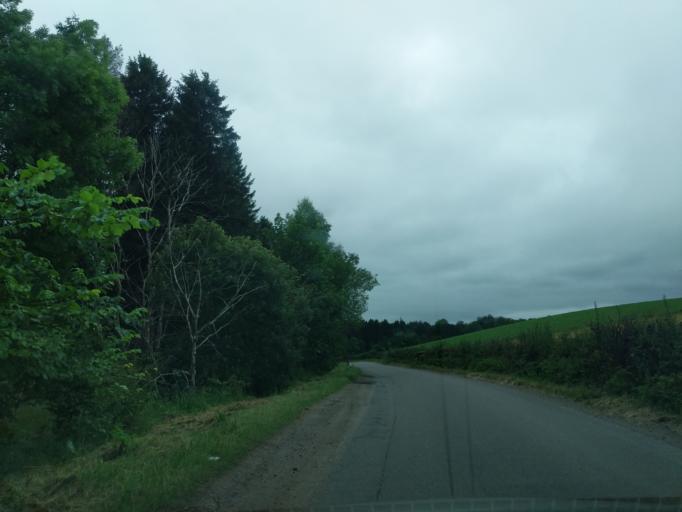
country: GB
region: Scotland
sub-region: Moray
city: Rothes
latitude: 57.4778
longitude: -3.1909
